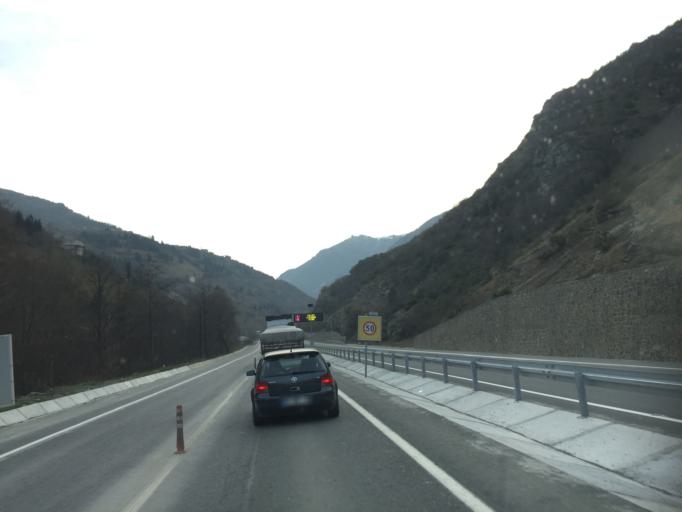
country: TR
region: Trabzon
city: Macka
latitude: 40.7938
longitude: 39.5825
